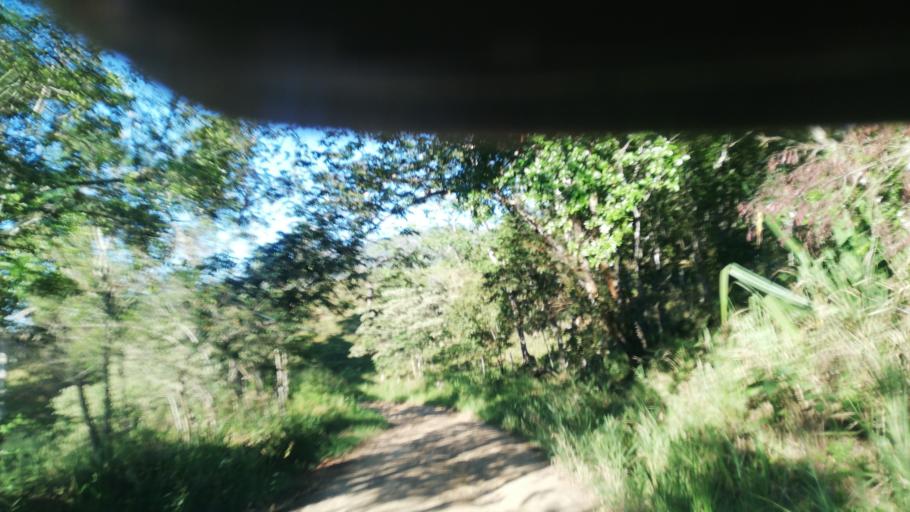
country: CO
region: Cundinamarca
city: Viani
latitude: 4.8344
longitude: -74.6192
